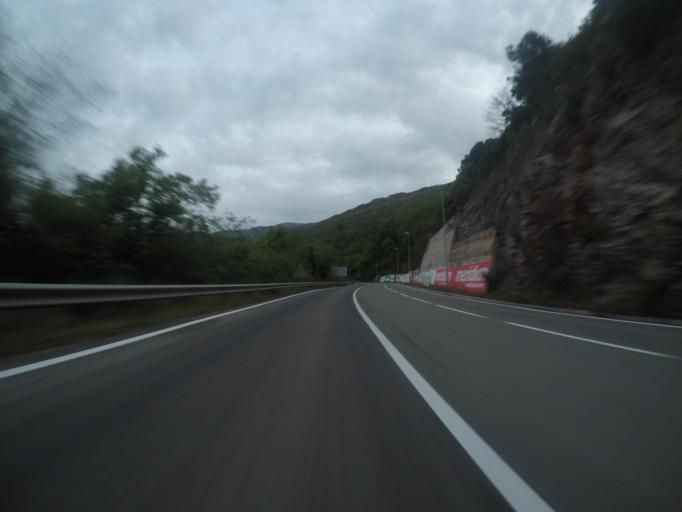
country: ME
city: Petrovac na Moru
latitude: 42.2057
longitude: 18.9499
